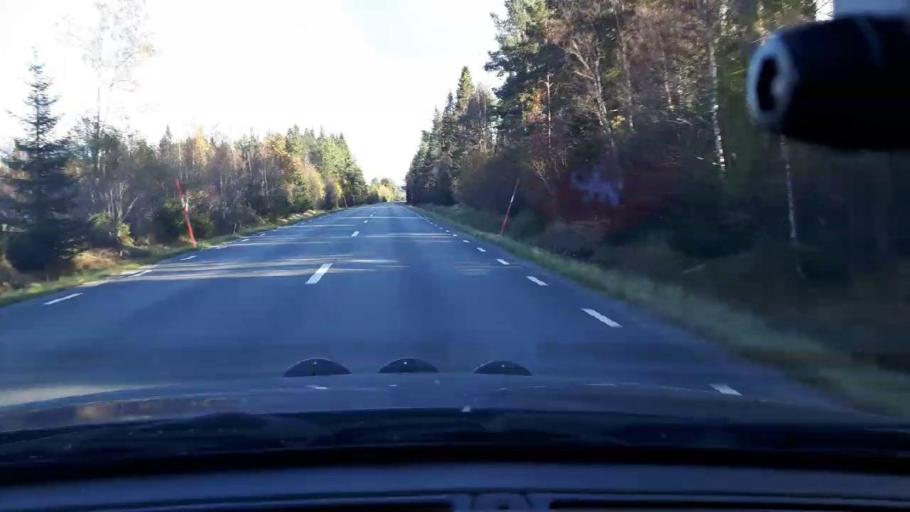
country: SE
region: Jaemtland
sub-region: Bergs Kommun
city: Hoverberg
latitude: 62.9849
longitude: 14.4421
